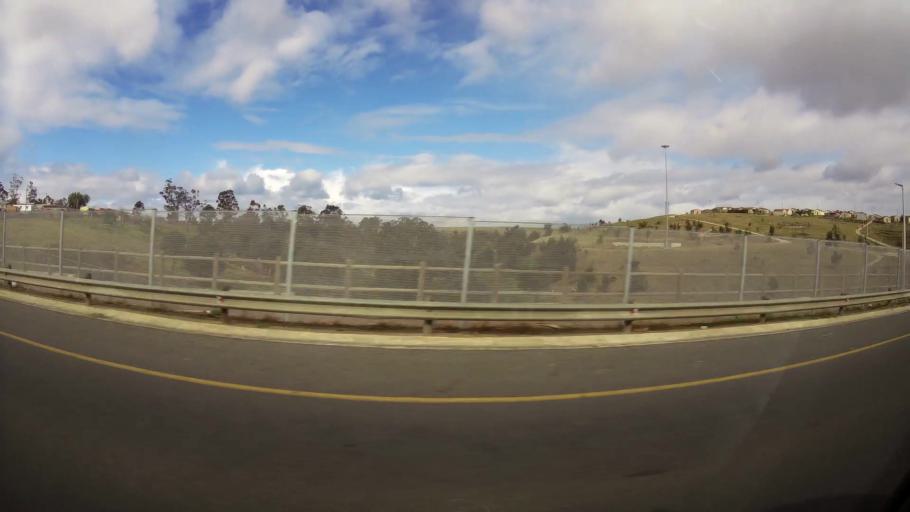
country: ZA
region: Western Cape
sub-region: Eden District Municipality
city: George
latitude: -33.9959
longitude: 22.4626
